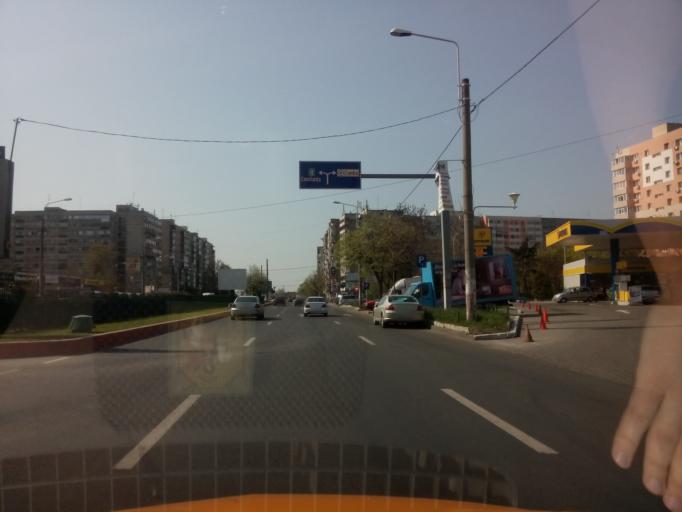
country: RO
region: Ilfov
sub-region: Comuna Popesti-Leordeni
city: Popesti-Leordeni
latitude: 44.4146
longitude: 26.1643
